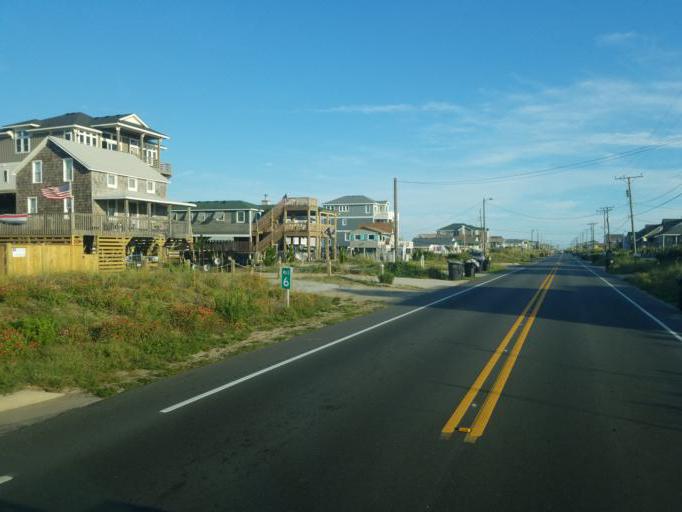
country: US
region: North Carolina
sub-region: Dare County
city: Kill Devil Hills
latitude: 36.0443
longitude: -75.6755
